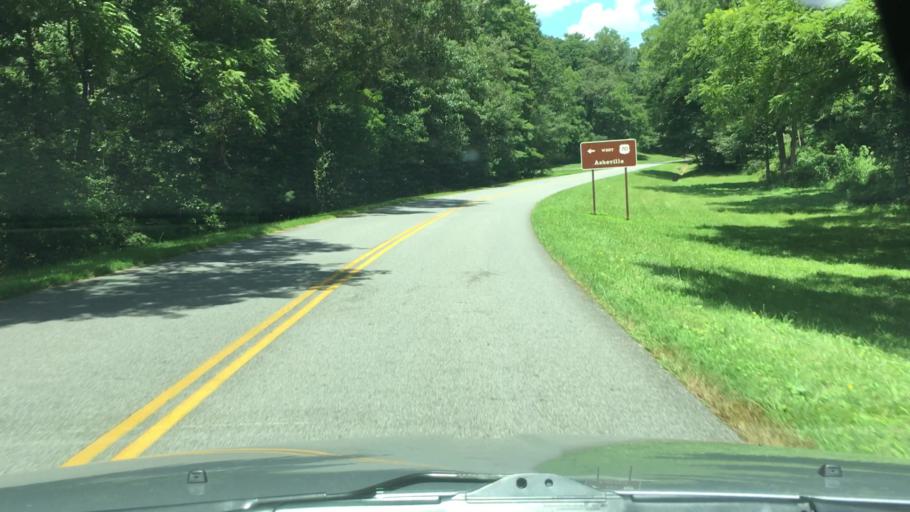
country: US
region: North Carolina
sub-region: Buncombe County
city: Biltmore Forest
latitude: 35.5870
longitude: -82.4795
